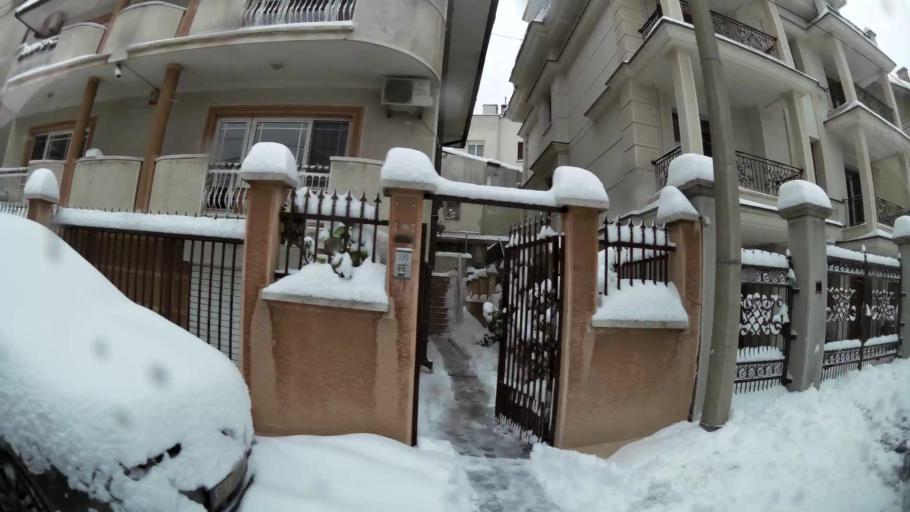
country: RS
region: Central Serbia
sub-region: Belgrade
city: Vracar
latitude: 44.7895
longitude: 20.4745
